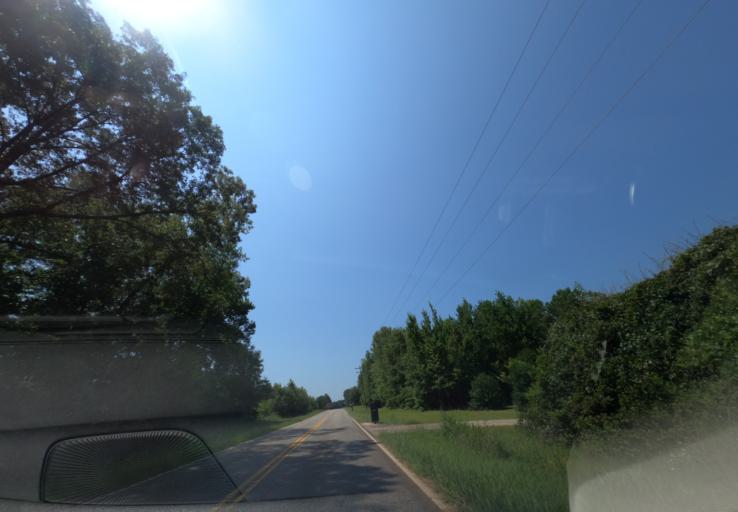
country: US
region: South Carolina
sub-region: Greenwood County
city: Greenwood
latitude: 34.0349
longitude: -82.1294
